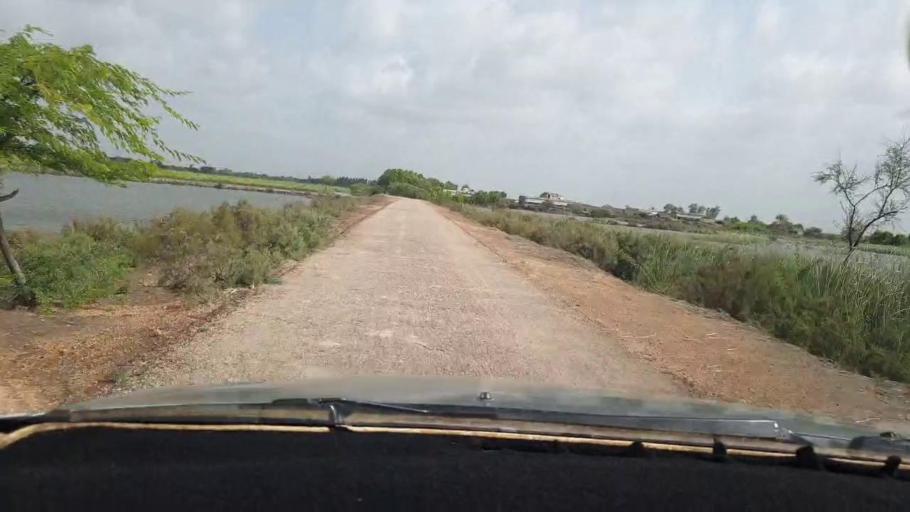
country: PK
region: Sindh
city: Tando Bago
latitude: 24.7872
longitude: 69.0283
